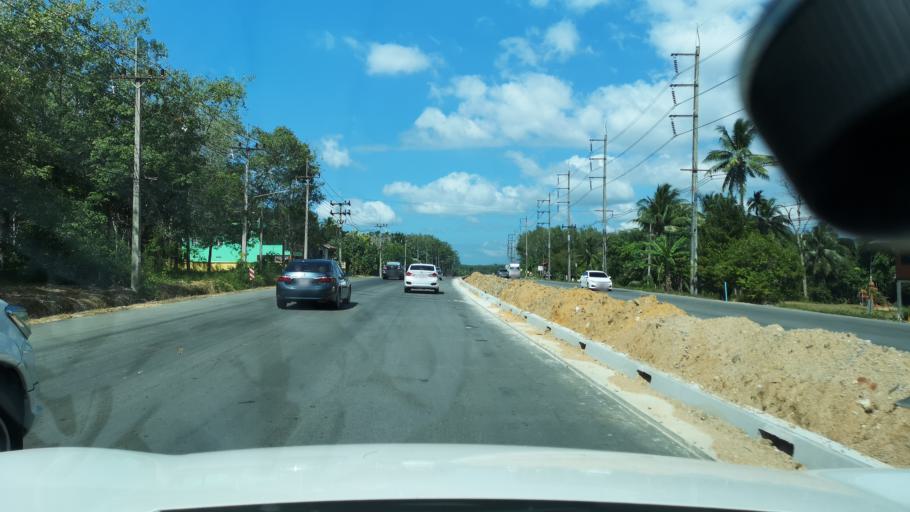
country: TH
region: Phangnga
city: Thai Mueang
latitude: 8.4366
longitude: 98.2570
